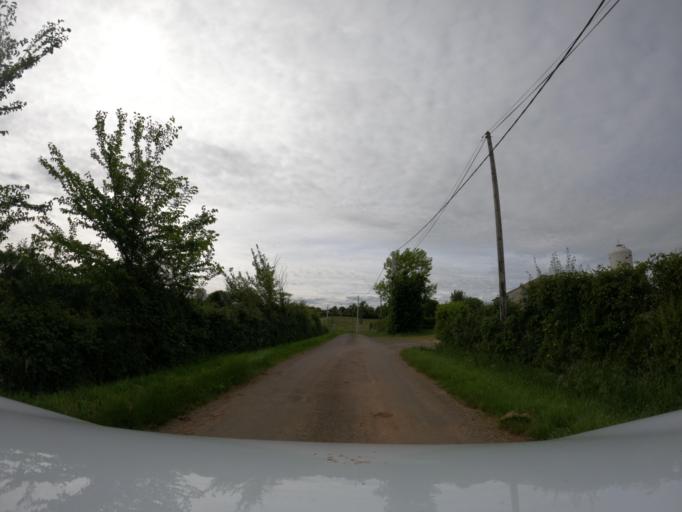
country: FR
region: Pays de la Loire
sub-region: Departement de la Vendee
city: Saint-Hilaire-des-Loges
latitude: 46.4810
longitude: -0.6624
